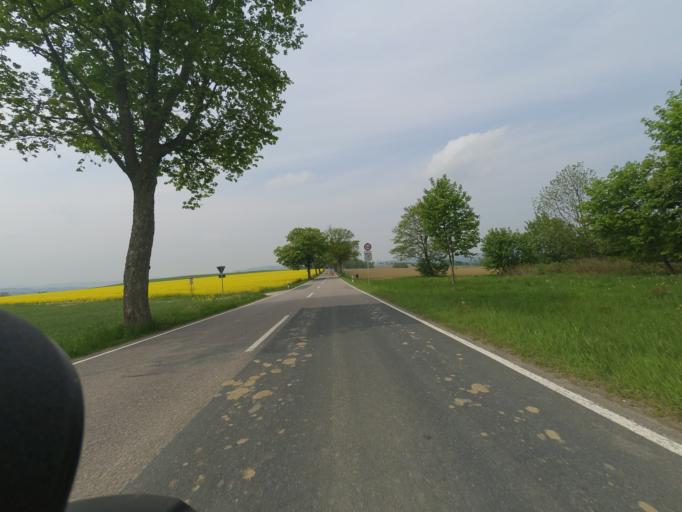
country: DE
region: Saxony
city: Grossruckerswalde
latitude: 50.6471
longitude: 13.1026
